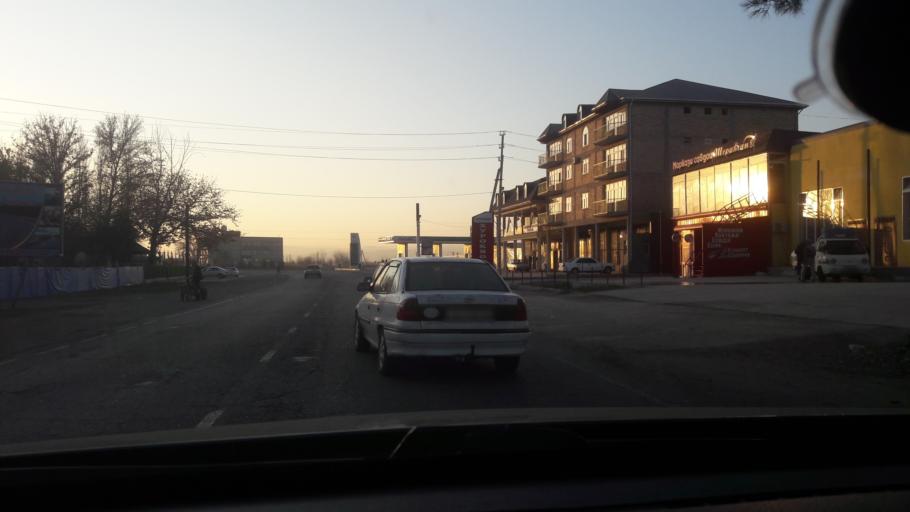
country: TJ
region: Khatlon
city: Vose'
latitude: 37.8052
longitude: 69.6221
